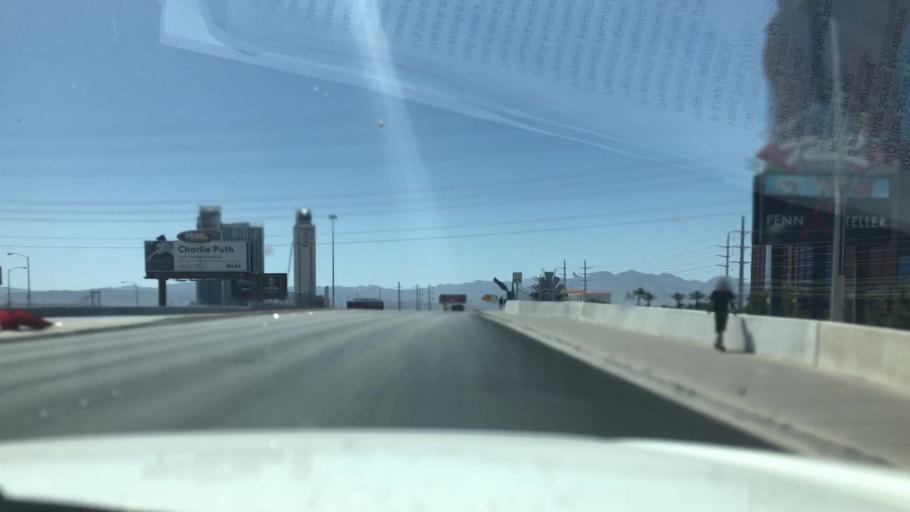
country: US
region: Nevada
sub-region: Clark County
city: Paradise
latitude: 36.1146
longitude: -115.1840
